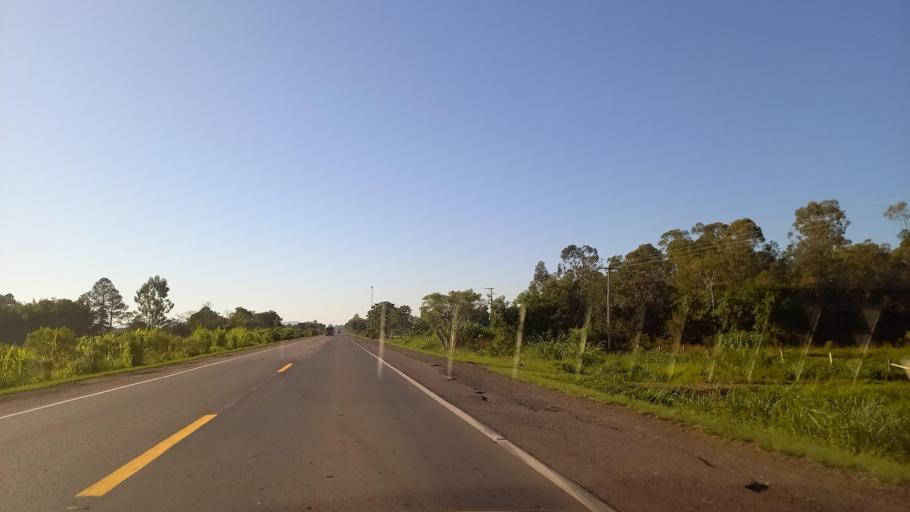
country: BR
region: Rio Grande do Sul
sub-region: Venancio Aires
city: Venancio Aires
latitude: -29.6631
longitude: -52.0616
